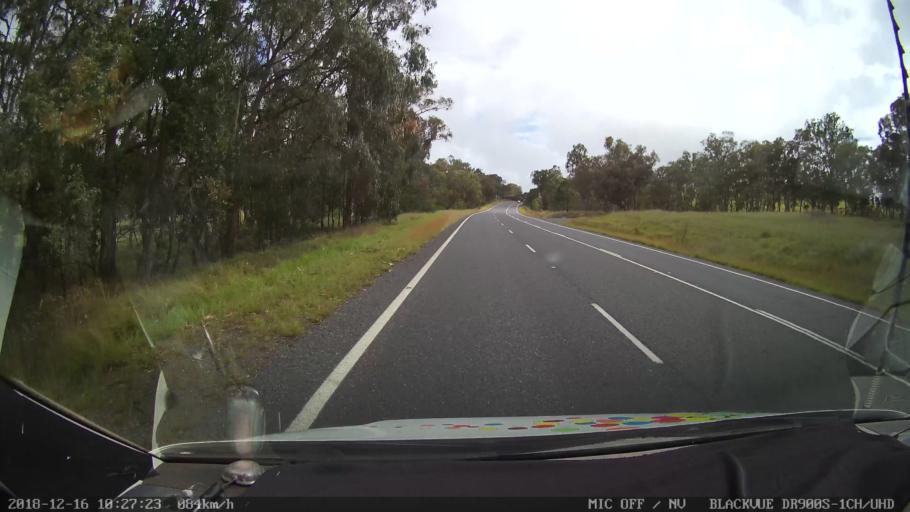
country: AU
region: New South Wales
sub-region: Tenterfield Municipality
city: Carrolls Creek
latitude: -29.1341
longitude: 151.9955
